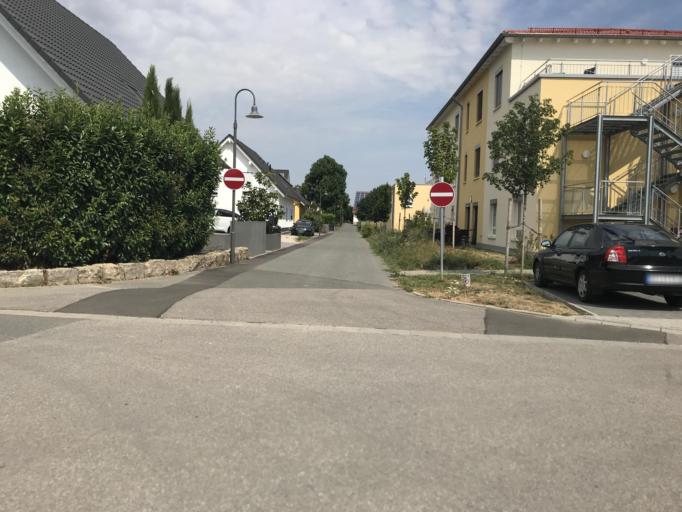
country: DE
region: Rheinland-Pfalz
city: Kongernheim
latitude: 49.8397
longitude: 8.2392
